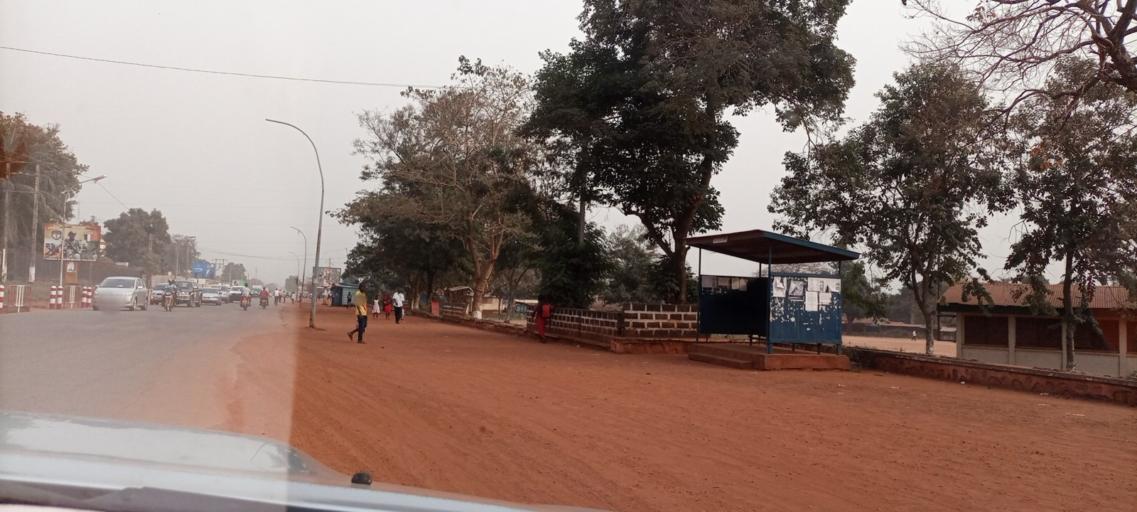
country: CF
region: Bangui
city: Bangui
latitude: 4.3730
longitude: 18.5726
